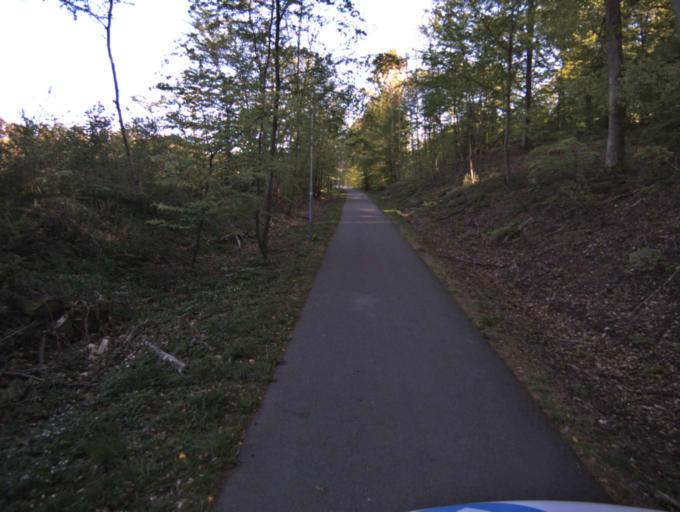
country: SE
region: Skane
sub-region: Kristianstads Kommun
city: Degeberga
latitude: 55.8343
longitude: 14.0794
